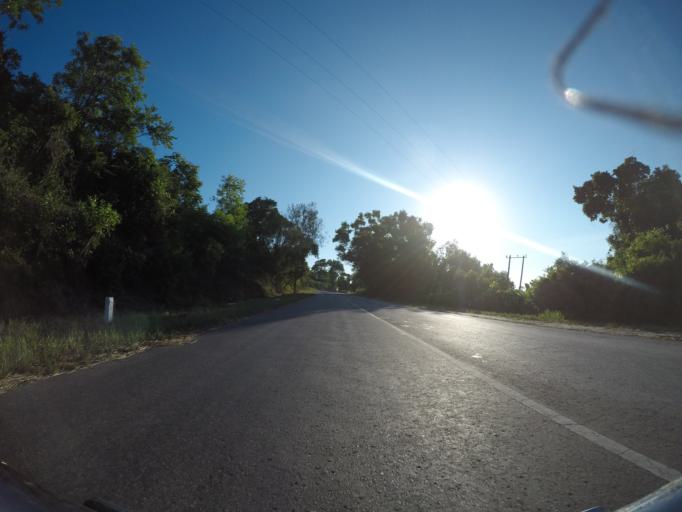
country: TZ
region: Pemba South
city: Uwelini
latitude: -5.3757
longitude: 39.6732
